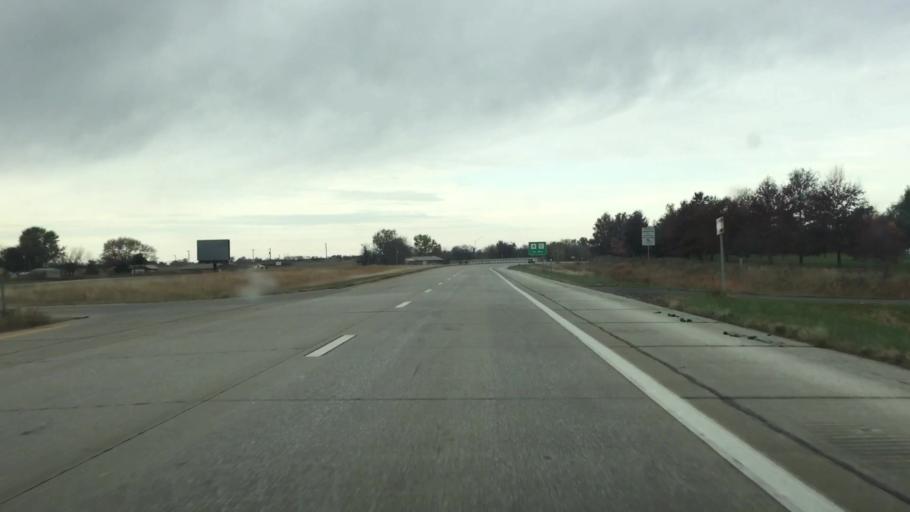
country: US
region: Missouri
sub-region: Saint Clair County
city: Osceola
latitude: 38.1423
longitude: -93.7200
